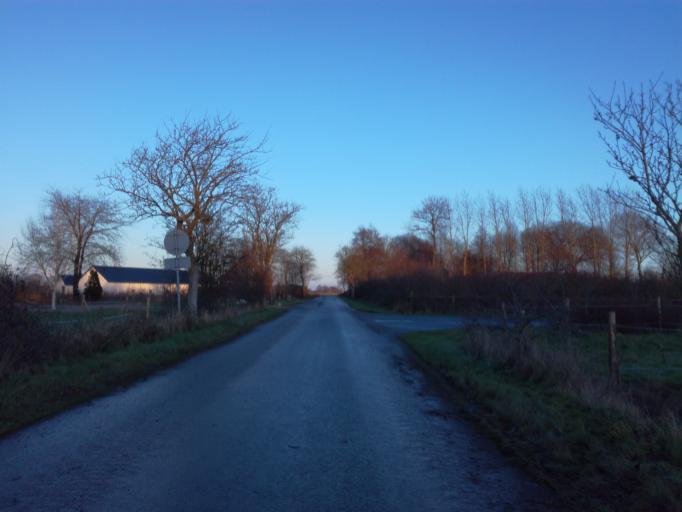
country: DK
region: South Denmark
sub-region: Fredericia Kommune
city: Taulov
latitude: 55.5531
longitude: 9.6419
